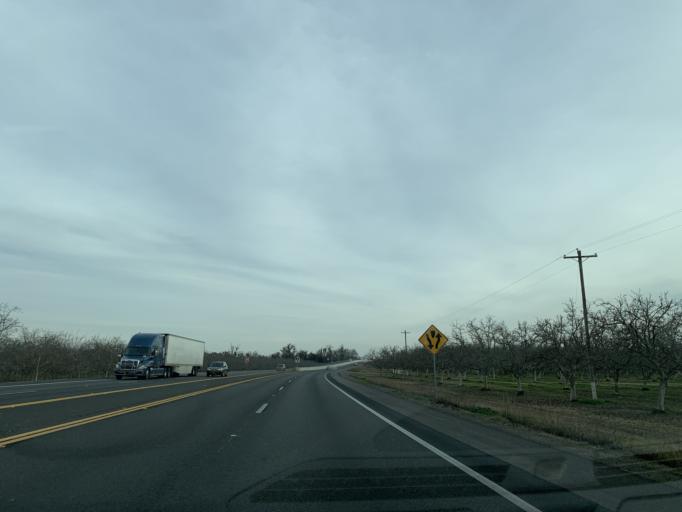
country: US
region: California
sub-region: Yuba County
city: Plumas Lake
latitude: 38.9099
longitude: -121.5963
